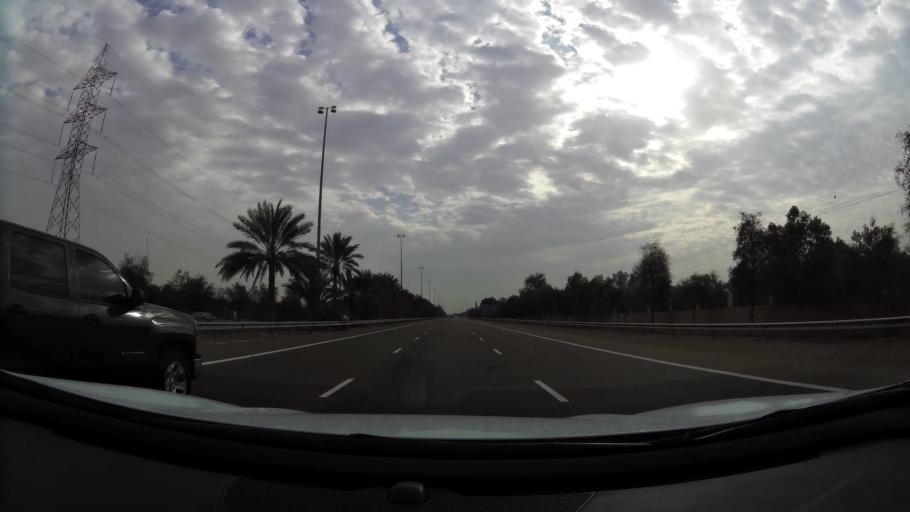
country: AE
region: Abu Dhabi
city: Al Ain
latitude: 24.2039
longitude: 55.4110
